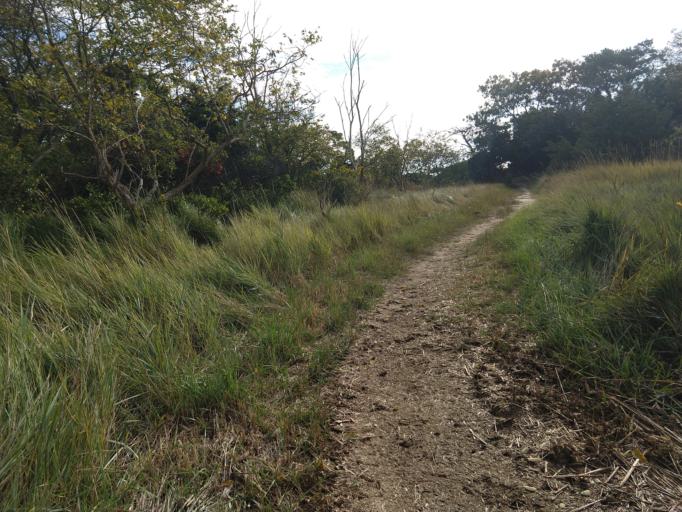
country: US
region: Massachusetts
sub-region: Barnstable County
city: North Eastham
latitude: 41.8785
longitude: -70.0036
